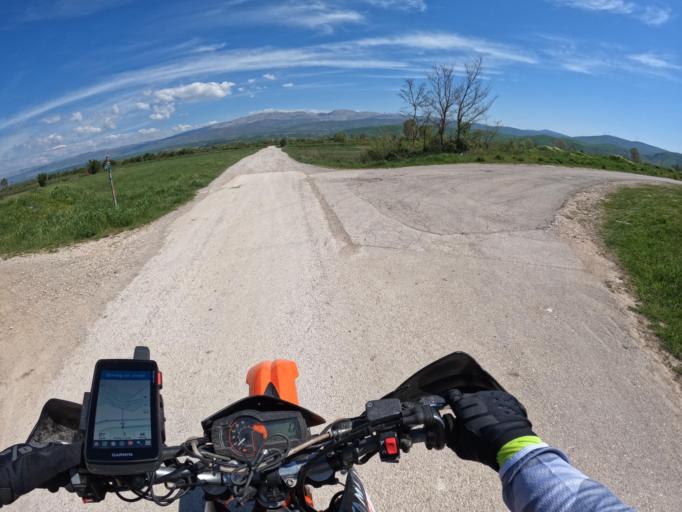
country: HR
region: Splitsko-Dalmatinska
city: Kosute
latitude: 43.6400
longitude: 16.7161
